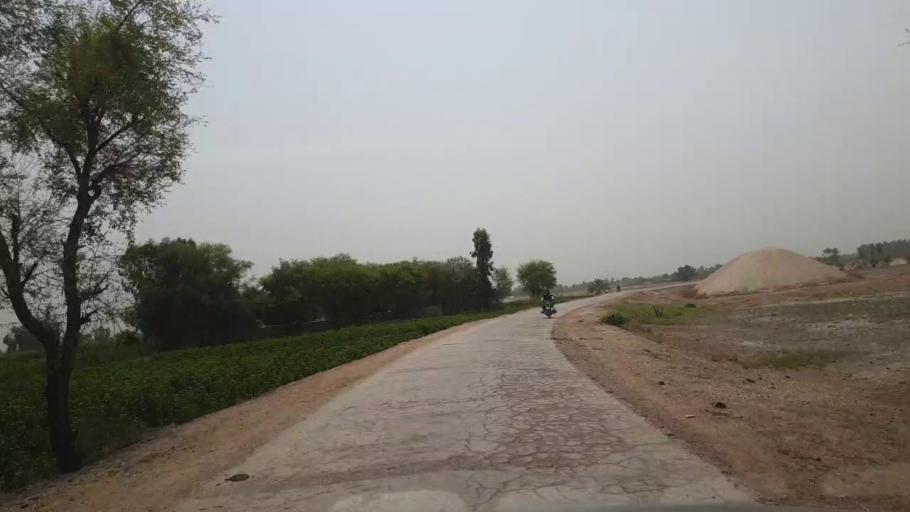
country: PK
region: Sindh
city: Gambat
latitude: 27.4418
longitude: 68.5181
